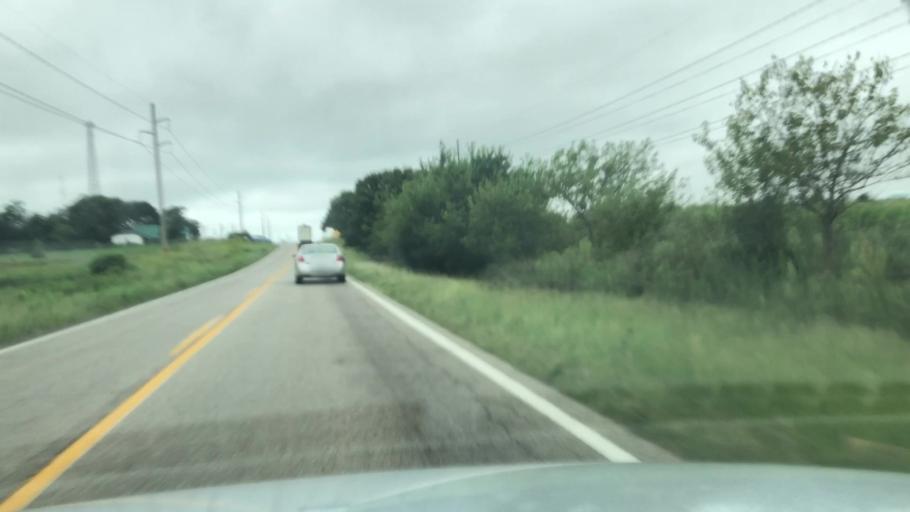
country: US
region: Oklahoma
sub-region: Washington County
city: Dewey
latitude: 36.7280
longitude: -95.8876
